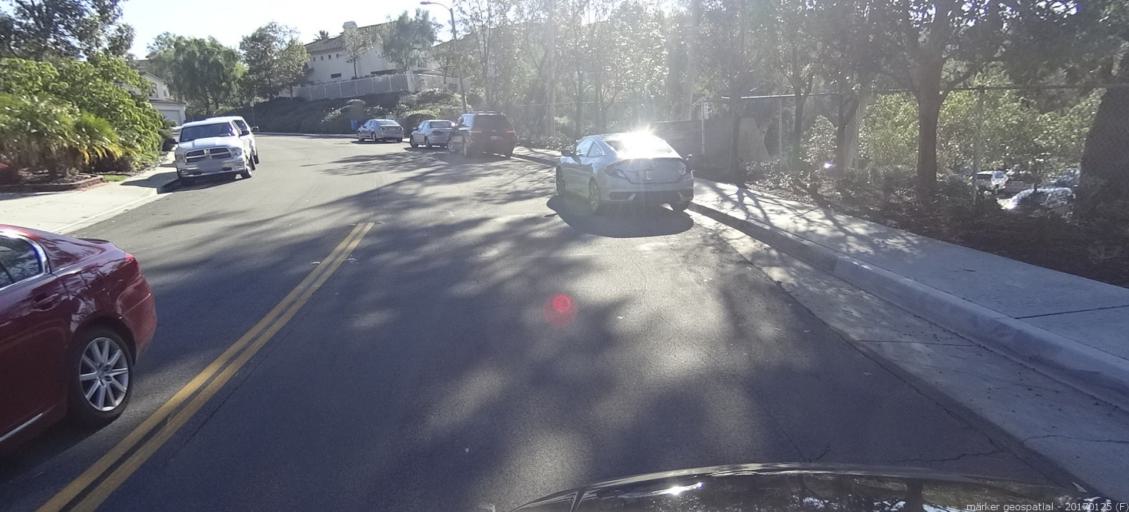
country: US
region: California
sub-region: Orange County
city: Portola Hills
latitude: 33.6809
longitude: -117.6313
